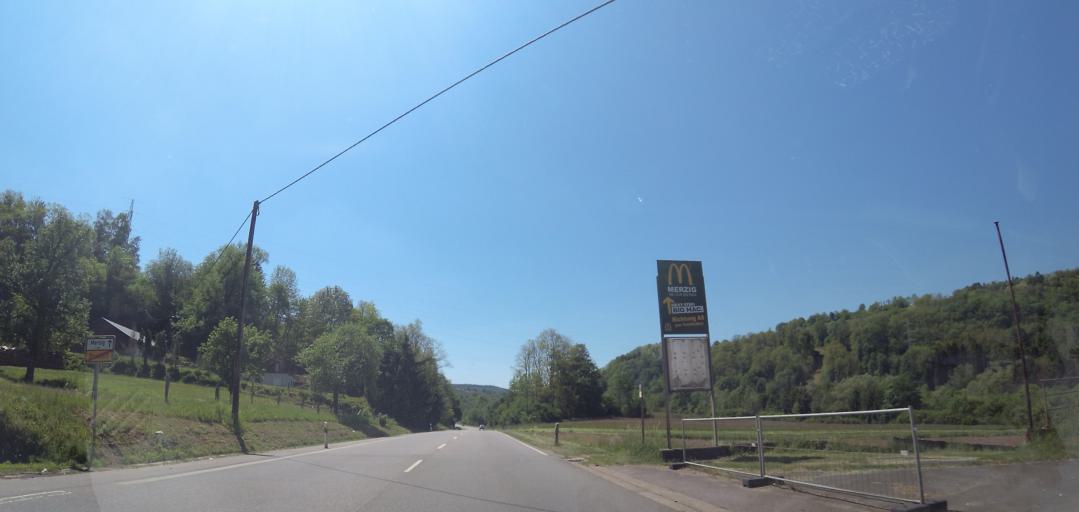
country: DE
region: Saarland
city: Merzig
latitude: 49.4599
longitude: 6.6762
